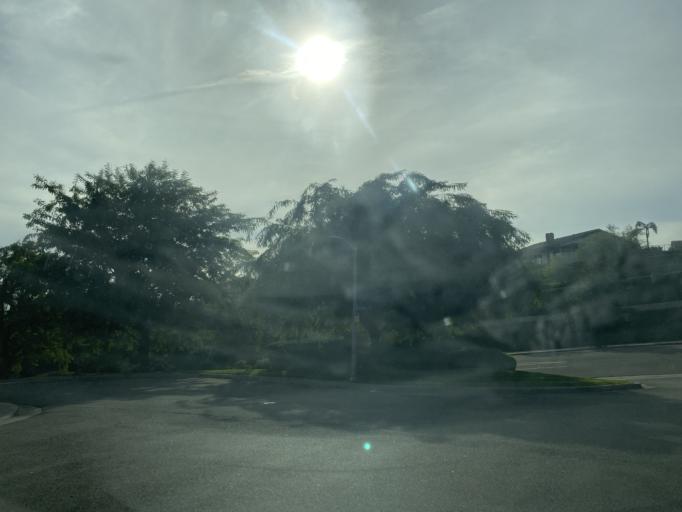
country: US
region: California
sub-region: Orange County
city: Brea
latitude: 33.8959
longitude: -117.8889
